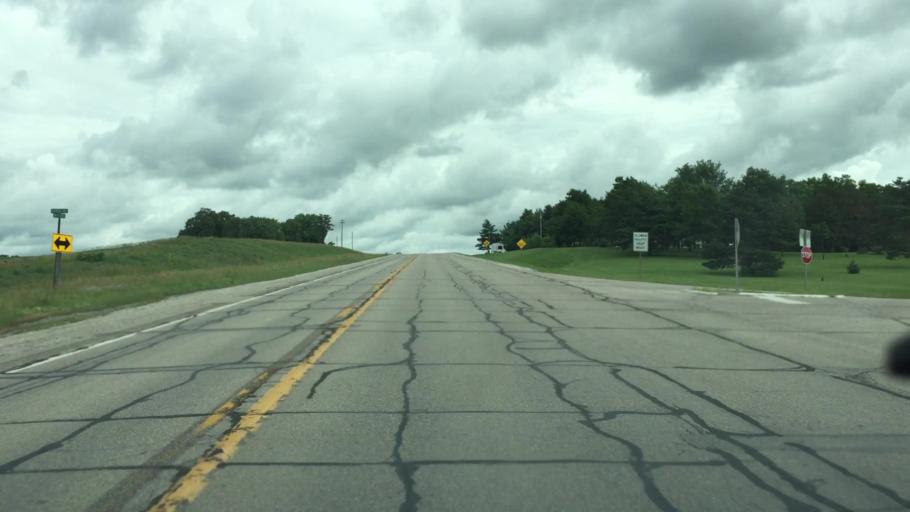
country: US
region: Iowa
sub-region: Jasper County
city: Monroe
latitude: 41.5434
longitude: -93.0984
